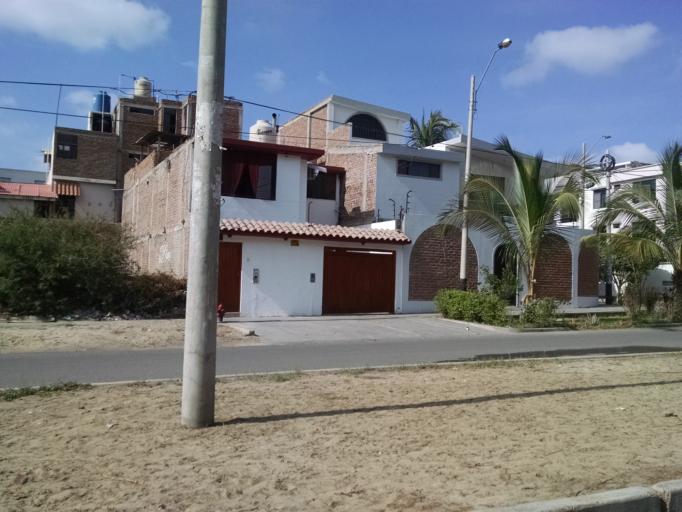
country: PE
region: Piura
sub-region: Provincia de Piura
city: Piura
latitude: -5.1705
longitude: -80.6334
